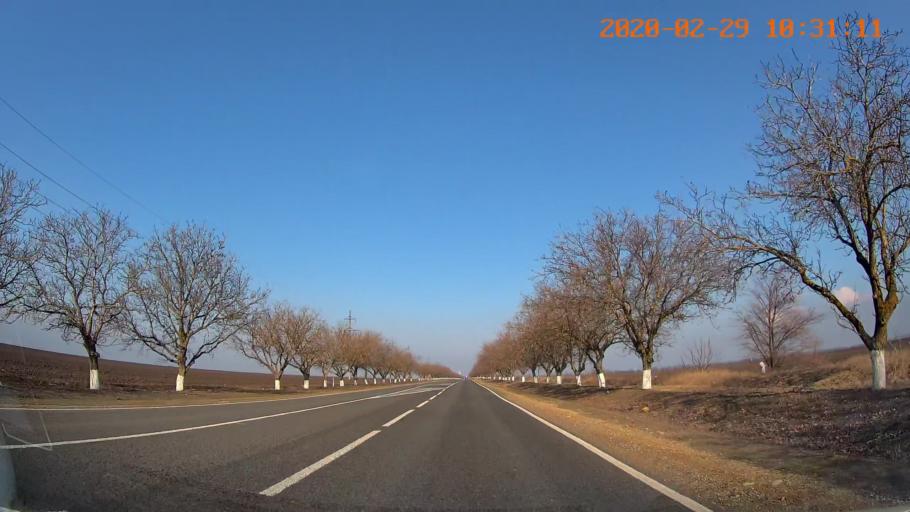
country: MD
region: Telenesti
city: Tiraspolul Nou
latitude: 46.9448
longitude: 29.5671
